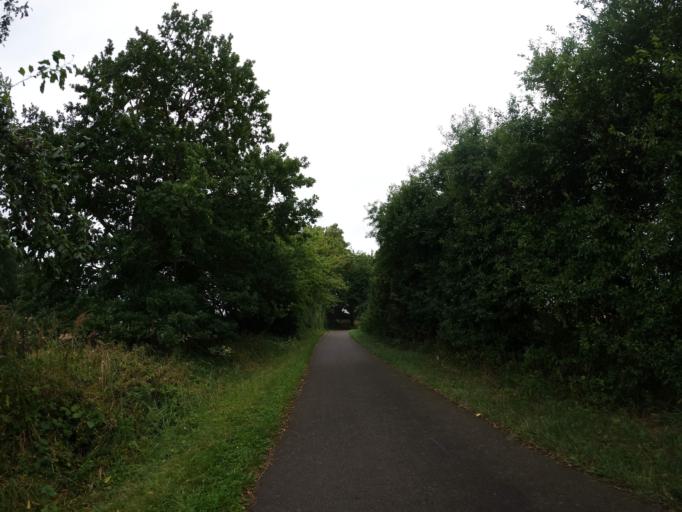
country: DE
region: Mecklenburg-Vorpommern
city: Poseritz
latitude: 54.2917
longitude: 13.2761
